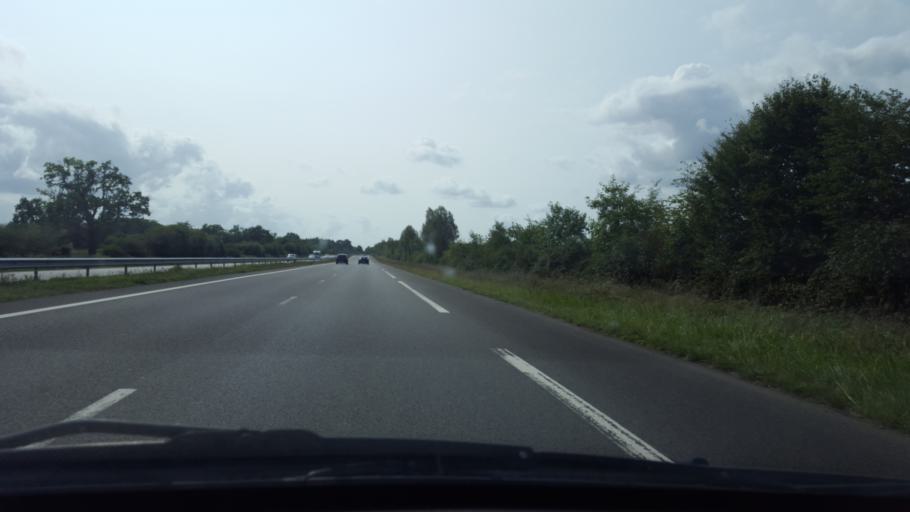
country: FR
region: Pays de la Loire
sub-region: Departement de la Loire-Atlantique
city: Saint-Lumine-de-Coutais
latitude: 47.0065
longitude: -1.7175
